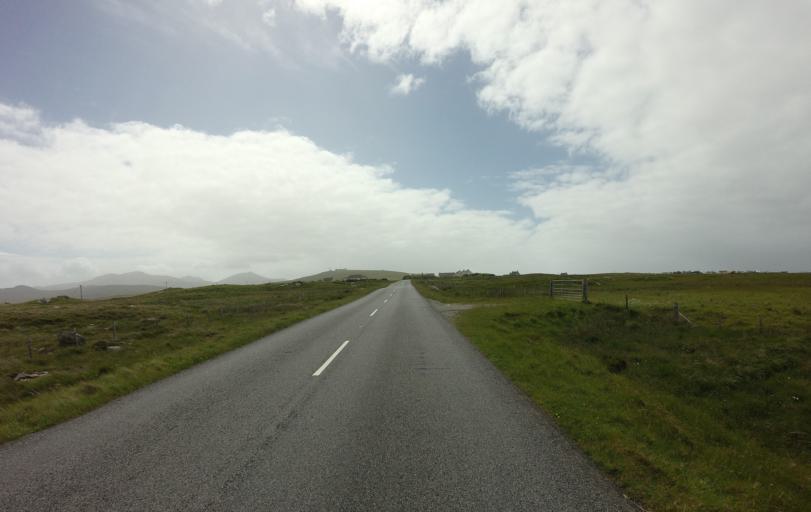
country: GB
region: Scotland
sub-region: Eilean Siar
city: Benbecula
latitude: 57.3566
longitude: -7.3571
